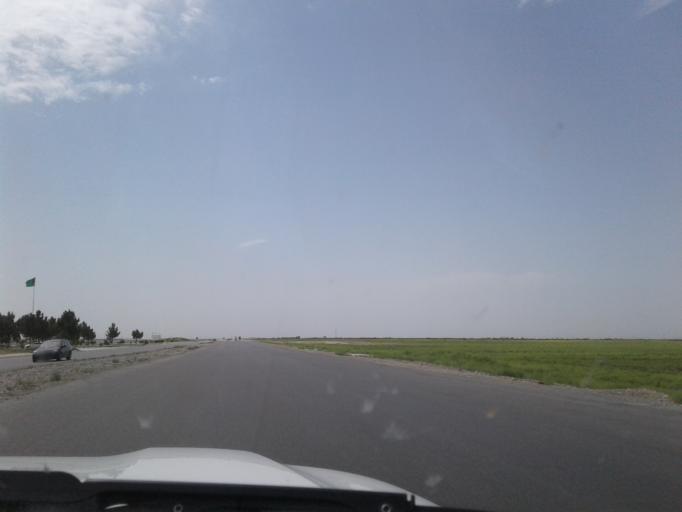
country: TM
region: Ahal
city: Kaka
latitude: 37.3716
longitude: 59.6112
